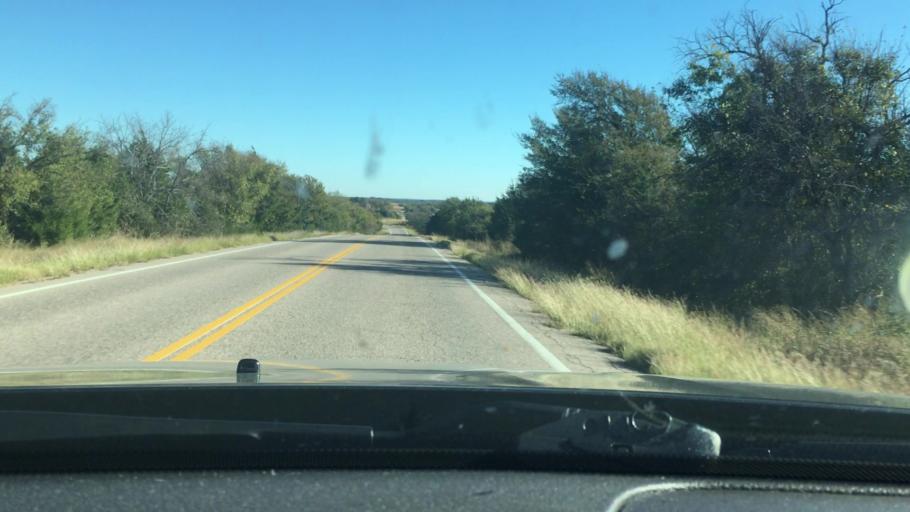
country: US
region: Oklahoma
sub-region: Marshall County
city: Madill
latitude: 34.1405
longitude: -96.7111
